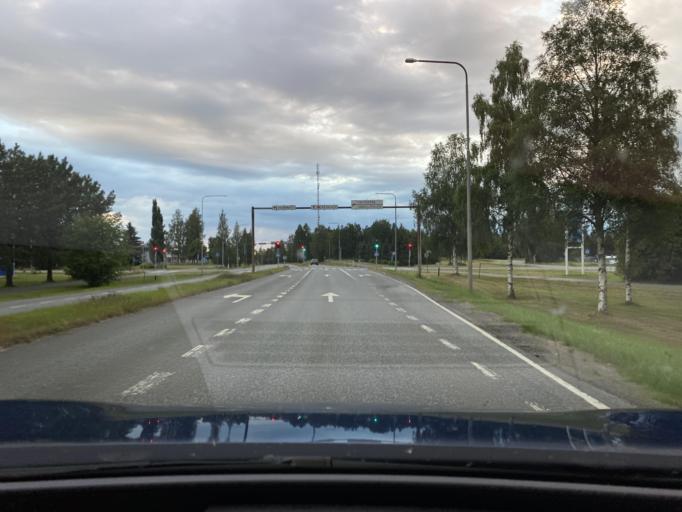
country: FI
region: Northern Ostrobothnia
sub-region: Raahe
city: Raahe
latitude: 64.6771
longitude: 24.4830
